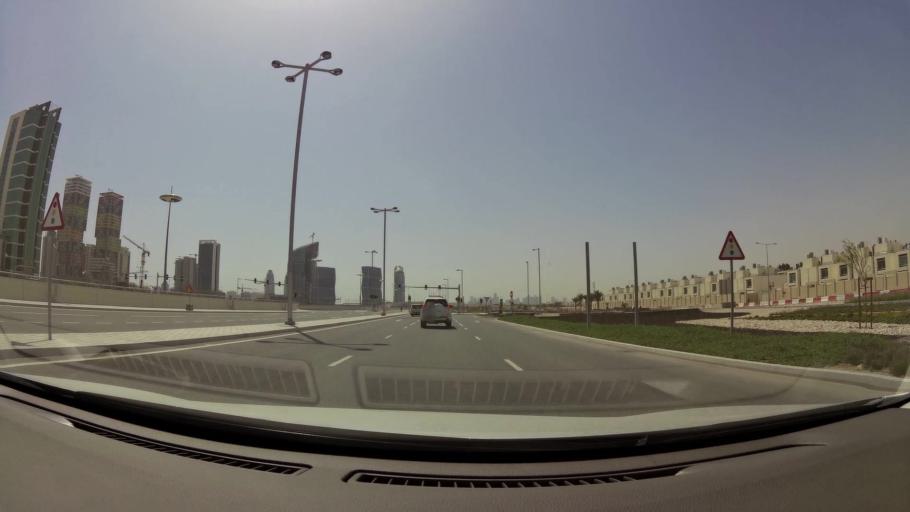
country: QA
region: Baladiyat ad Dawhah
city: Doha
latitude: 25.3895
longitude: 51.5177
